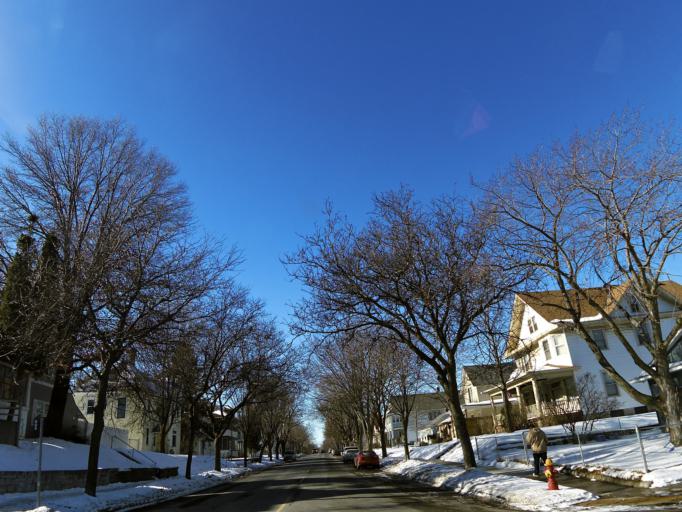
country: US
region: Minnesota
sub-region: Ramsey County
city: Saint Paul
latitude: 44.9631
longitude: -93.0507
